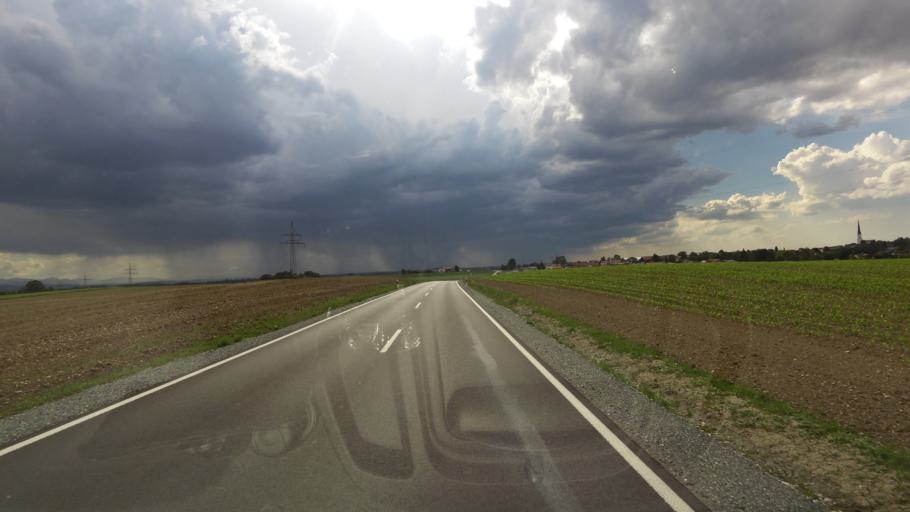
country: DE
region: Bavaria
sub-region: Upper Bavaria
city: Griesstatt
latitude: 47.9882
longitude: 12.1904
